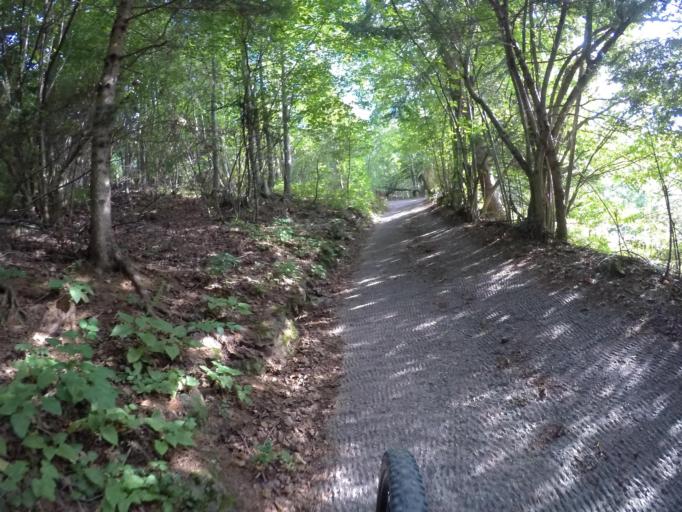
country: IT
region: Friuli Venezia Giulia
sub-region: Provincia di Udine
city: Paularo
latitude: 46.5408
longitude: 13.1122
